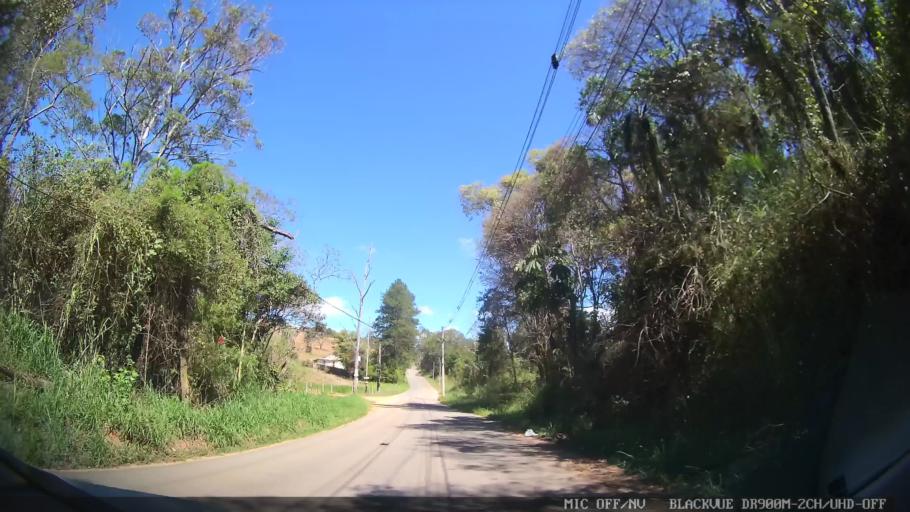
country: BR
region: Sao Paulo
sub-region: Campo Limpo Paulista
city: Campo Limpo Paulista
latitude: -23.1682
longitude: -46.7340
